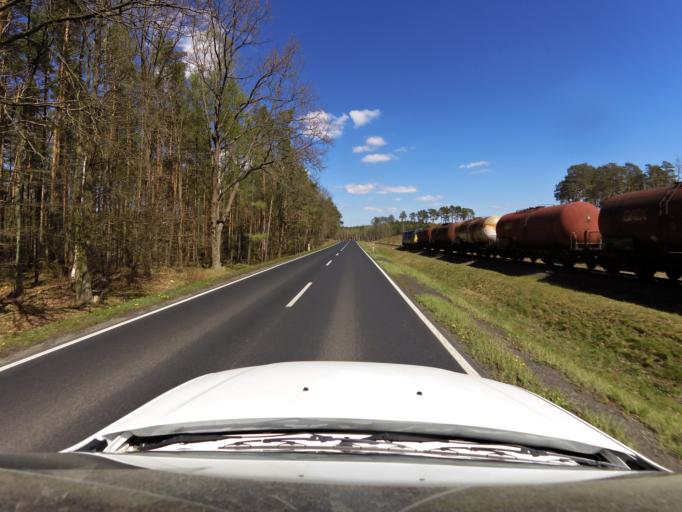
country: PL
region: West Pomeranian Voivodeship
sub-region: Powiat mysliborski
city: Debno
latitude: 52.7577
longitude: 14.7347
